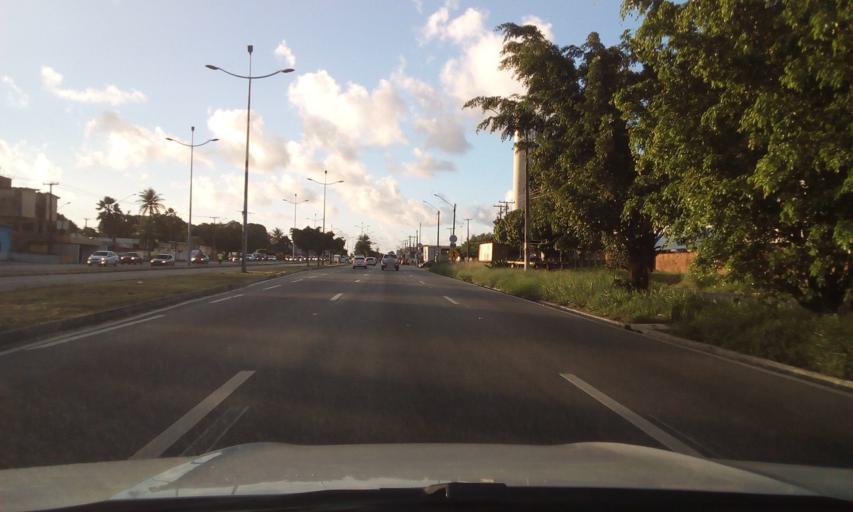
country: BR
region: Pernambuco
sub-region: Abreu E Lima
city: Abreu e Lima
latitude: -7.8769
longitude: -34.9055
